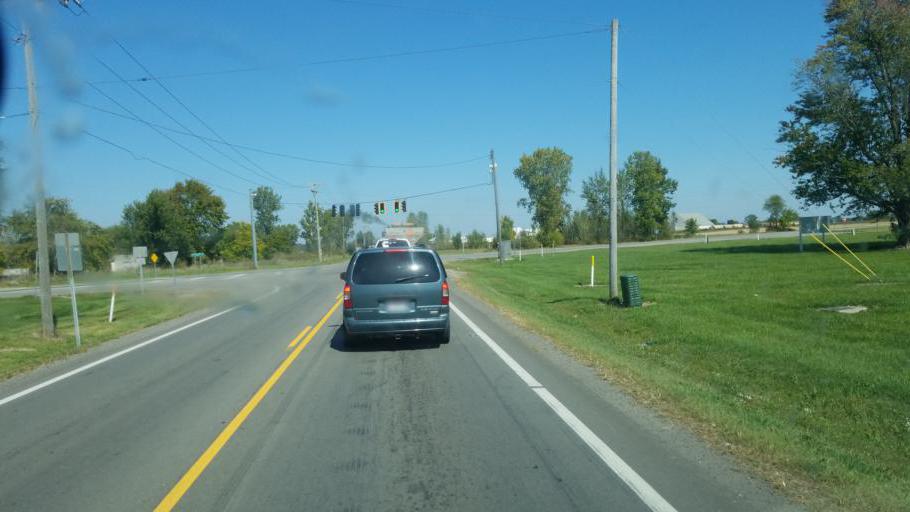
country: US
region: Ohio
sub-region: Marion County
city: Marion
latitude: 40.6147
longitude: -83.0302
